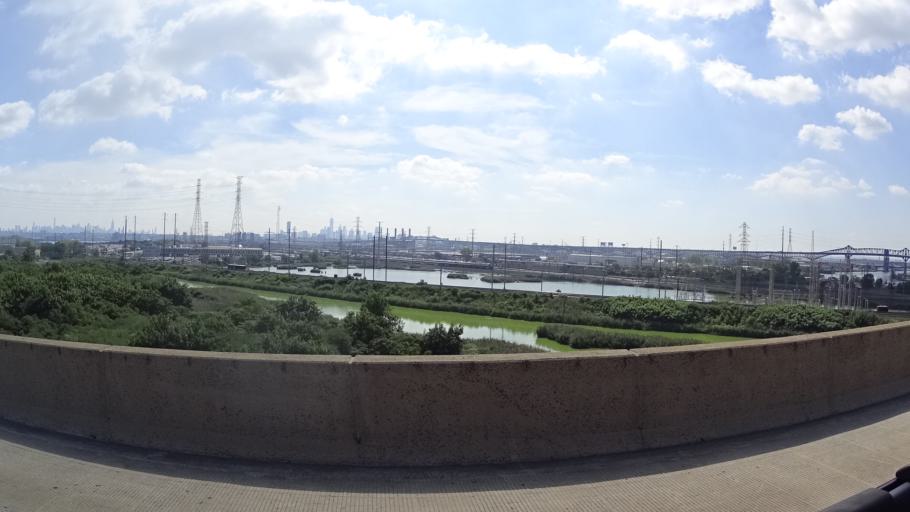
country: US
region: New Jersey
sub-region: Hudson County
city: Kearny
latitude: 40.7475
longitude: -74.1197
